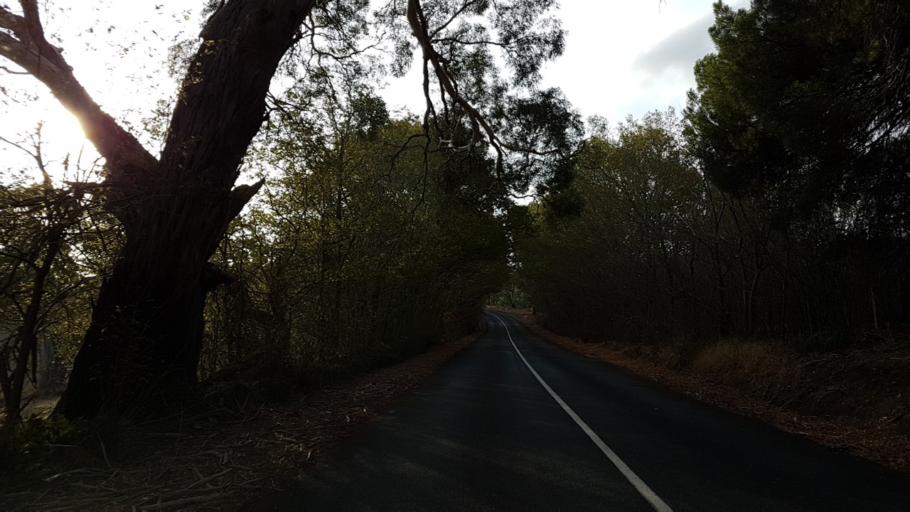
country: AU
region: South Australia
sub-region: Adelaide Hills
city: Woodside
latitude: -34.9805
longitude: 138.8942
